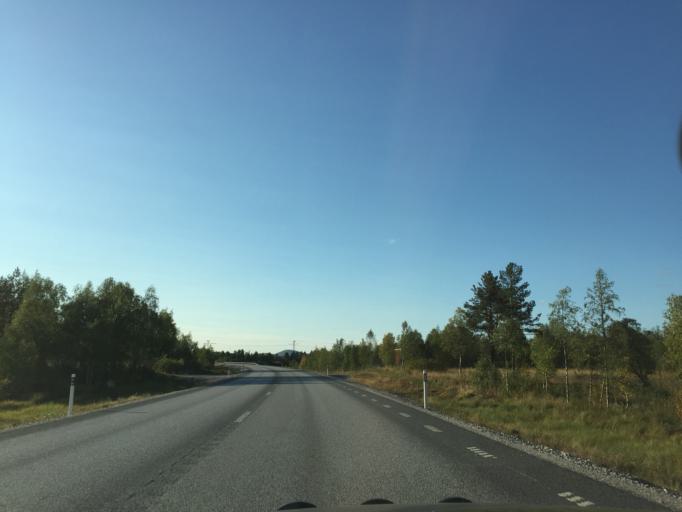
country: SE
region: Norrbotten
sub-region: Gallivare Kommun
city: Malmberget
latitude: 67.6428
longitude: 21.0548
